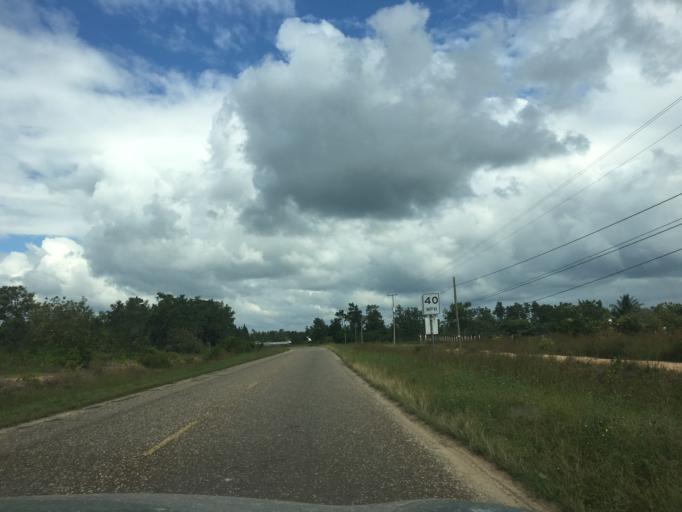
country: BZ
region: Stann Creek
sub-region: Dangriga
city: Dangriga
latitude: 16.8898
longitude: -88.3384
